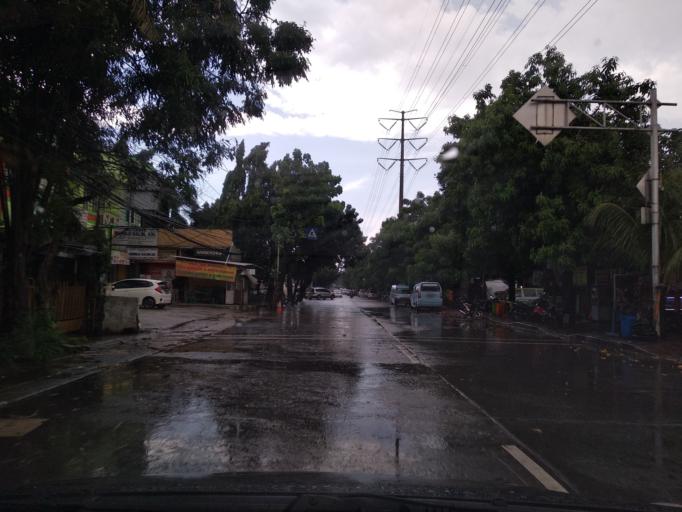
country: ID
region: Jakarta Raya
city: Jakarta
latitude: -6.2215
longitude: 106.8860
